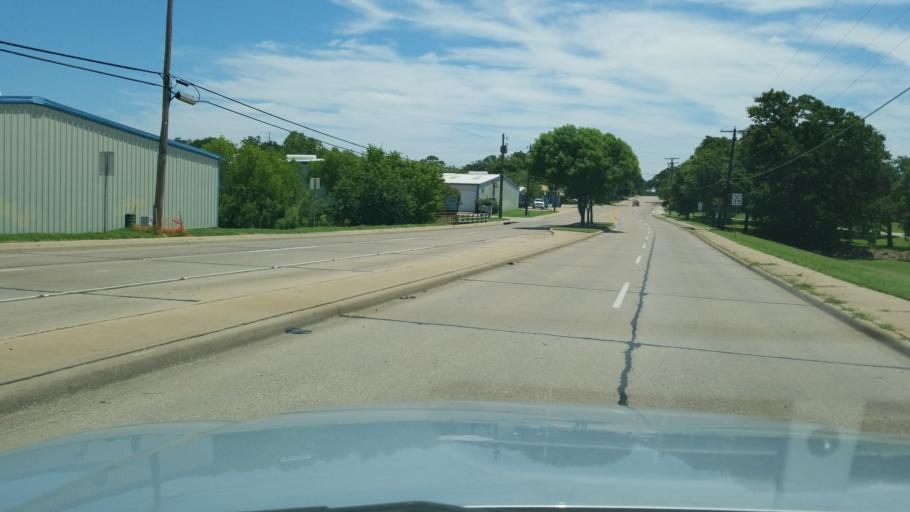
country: US
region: Texas
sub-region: Dallas County
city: Irving
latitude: 32.8012
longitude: -96.9169
